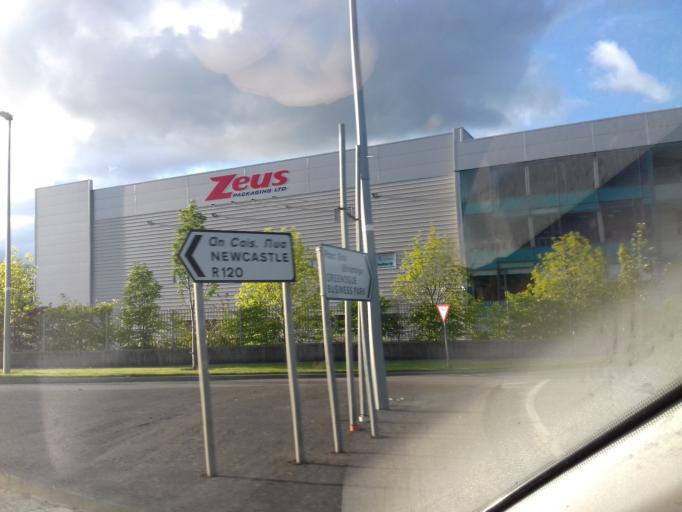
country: IE
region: Leinster
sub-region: South Dublin
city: Rathcoole
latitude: 53.2924
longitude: -6.4732
